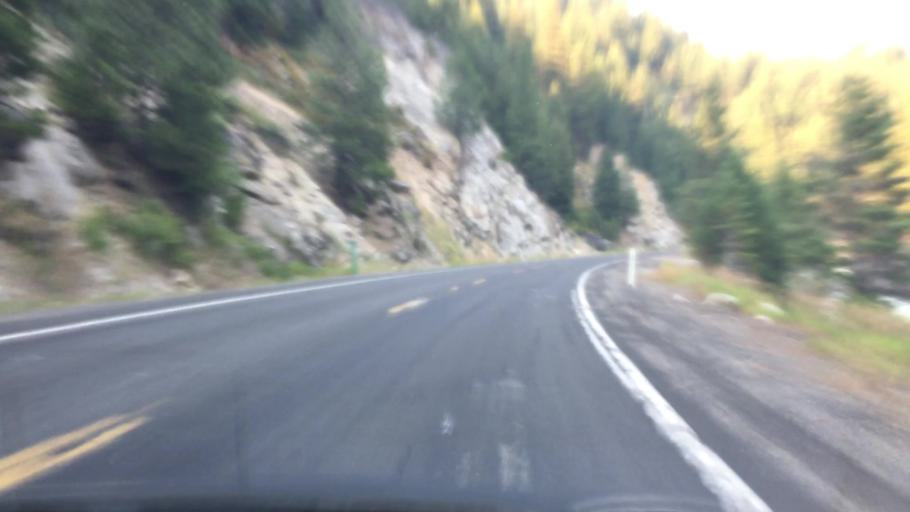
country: US
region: Idaho
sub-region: Valley County
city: Cascade
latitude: 44.2615
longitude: -116.0794
